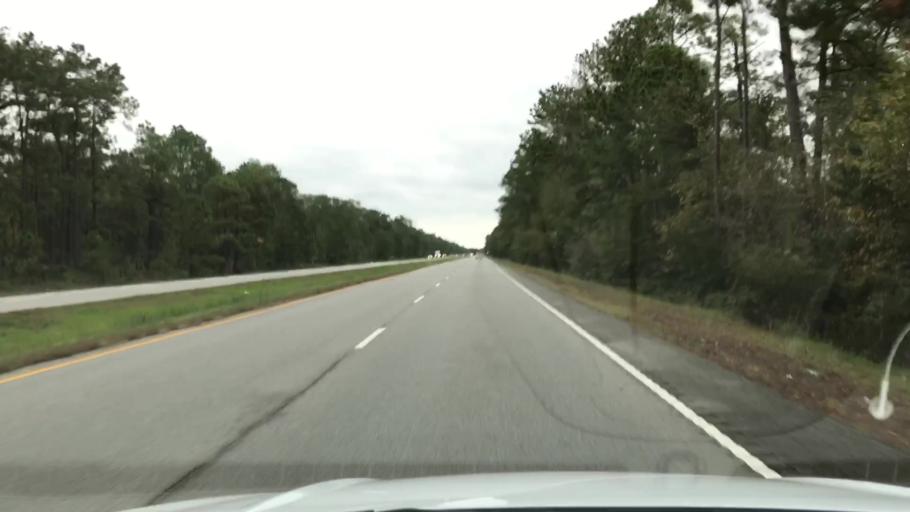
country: US
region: South Carolina
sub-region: Georgetown County
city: Georgetown
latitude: 33.4063
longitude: -79.1965
